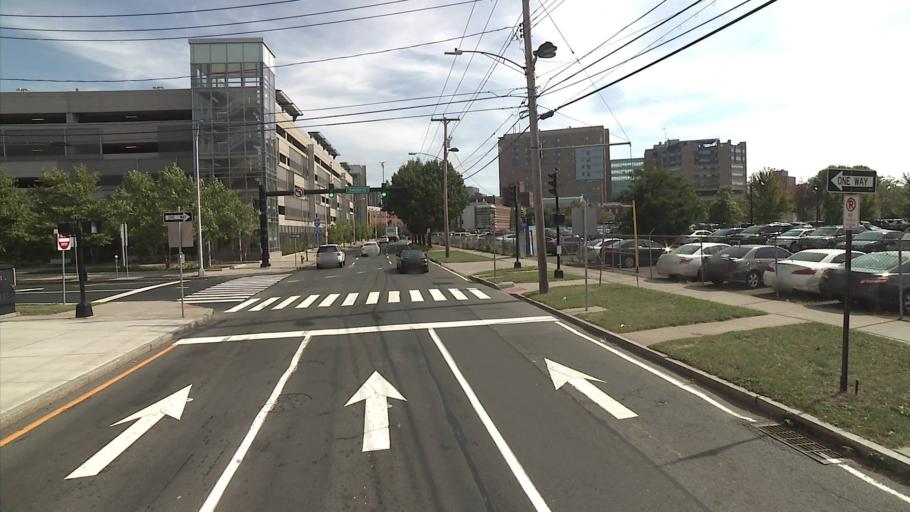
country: US
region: Connecticut
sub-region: New Haven County
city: New Haven
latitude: 41.3061
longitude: -72.9395
